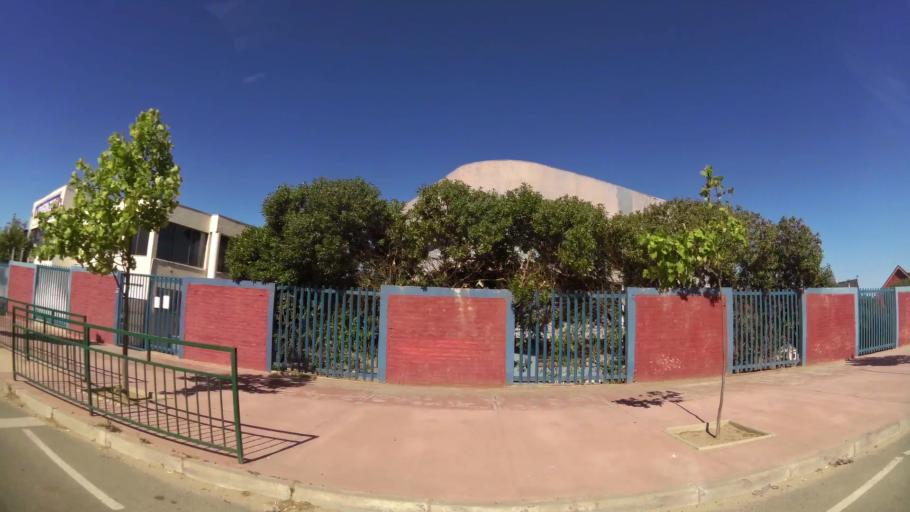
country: CL
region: Valparaiso
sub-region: Provincia de Valparaiso
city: Valparaiso
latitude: -33.1271
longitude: -71.5715
